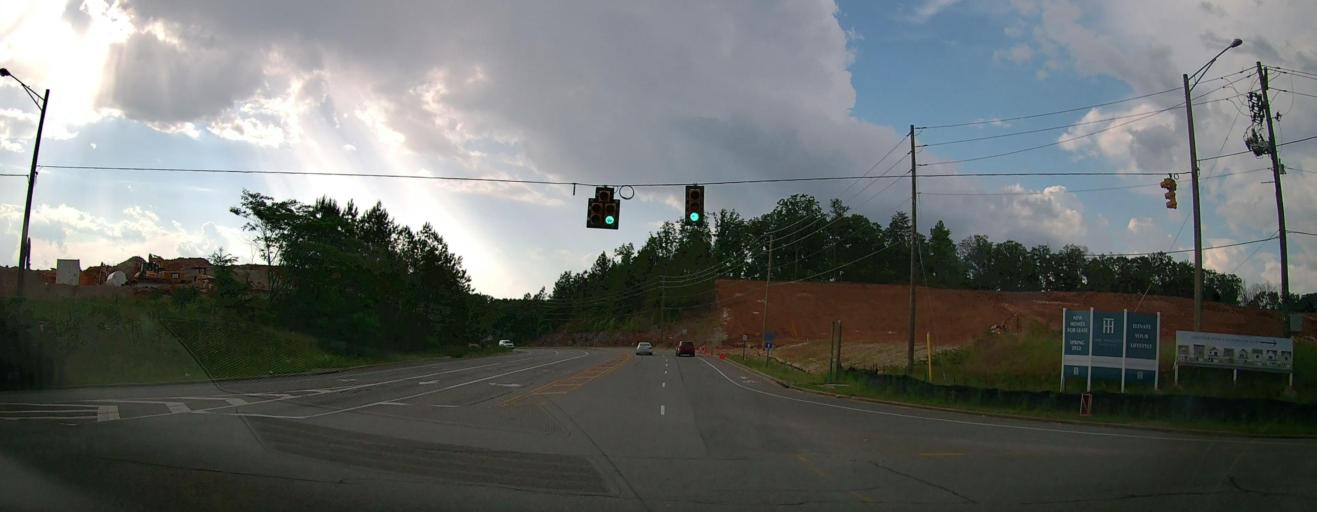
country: US
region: Alabama
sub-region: Jefferson County
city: Irondale
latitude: 33.5352
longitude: -86.6734
